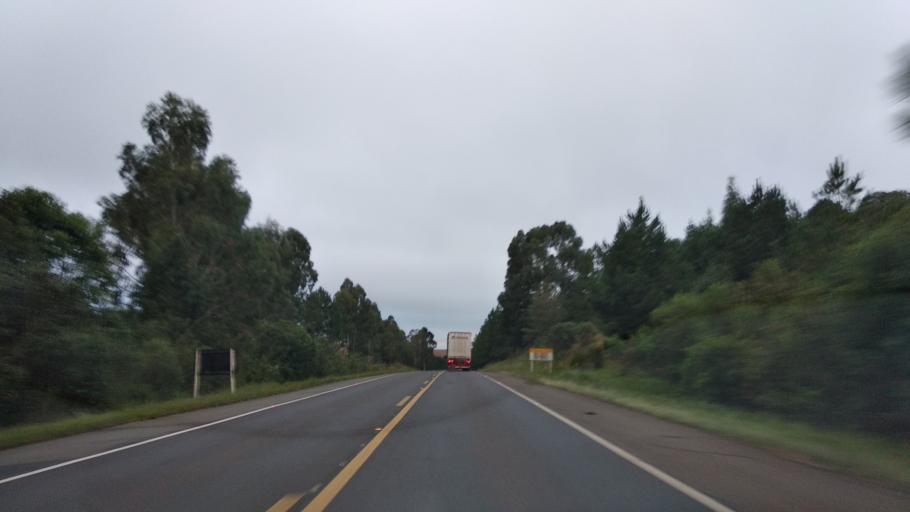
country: BR
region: Santa Catarina
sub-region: Campos Novos
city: Campos Novos
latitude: -27.3795
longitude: -51.0966
